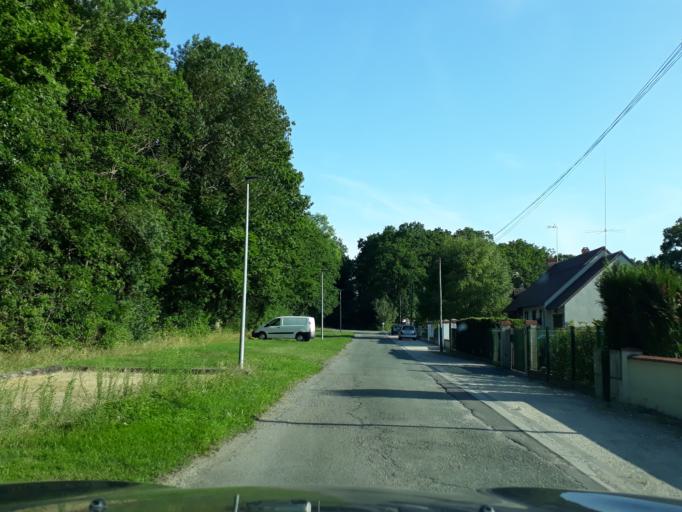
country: FR
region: Centre
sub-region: Departement du Loiret
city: Chaingy
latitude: 47.9274
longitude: 1.7434
